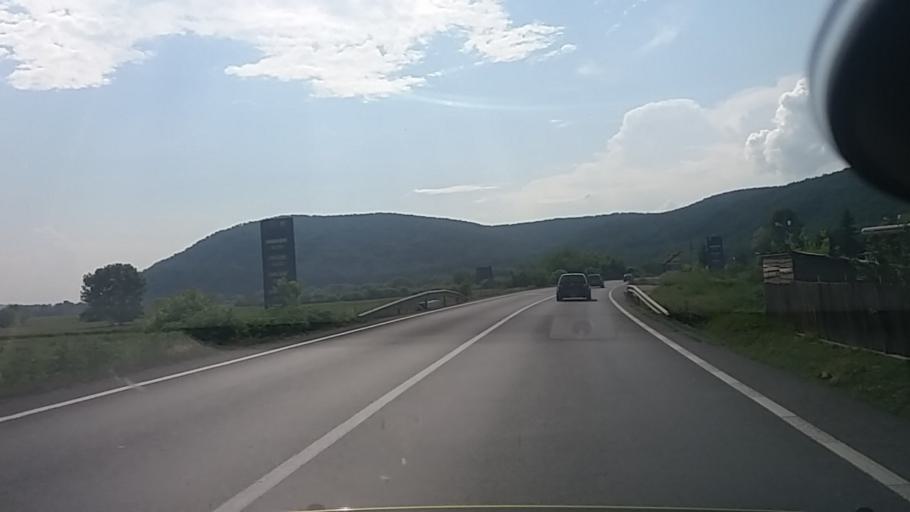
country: RO
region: Arad
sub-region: Comuna Barzava
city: Barzava
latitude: 46.1116
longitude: 21.9671
